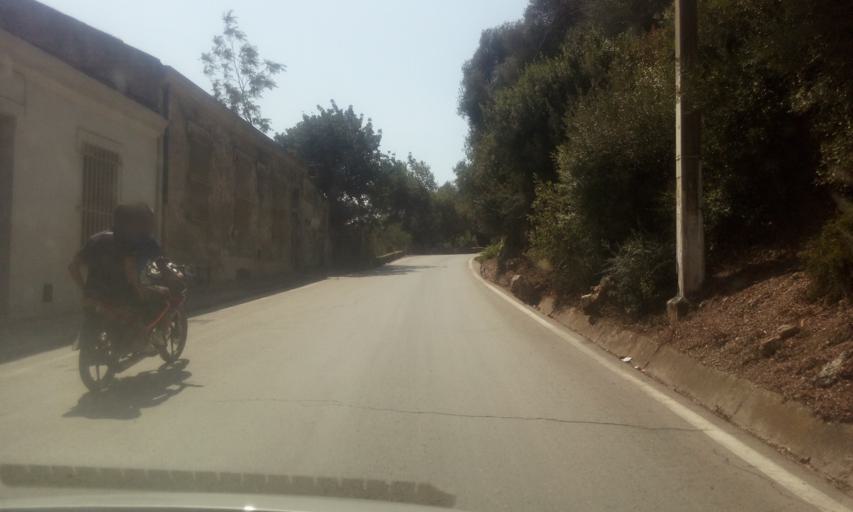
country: DZ
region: Bejaia
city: Bejaia
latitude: 36.7563
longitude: 5.0924
